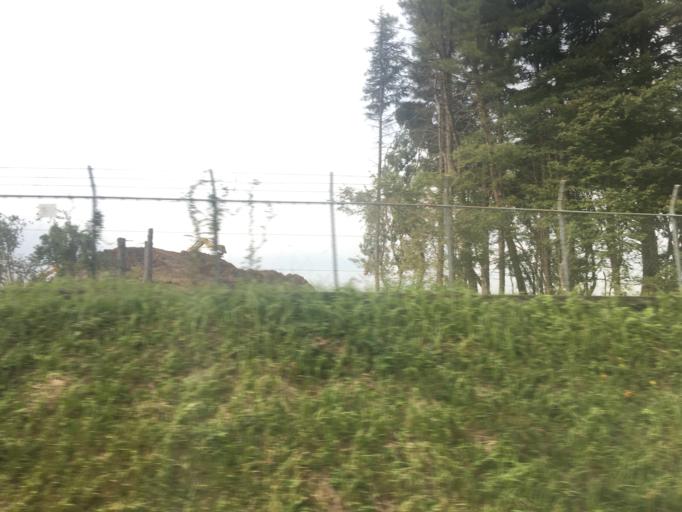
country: JP
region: Saitama
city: Sayama
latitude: 35.8439
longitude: 139.4190
